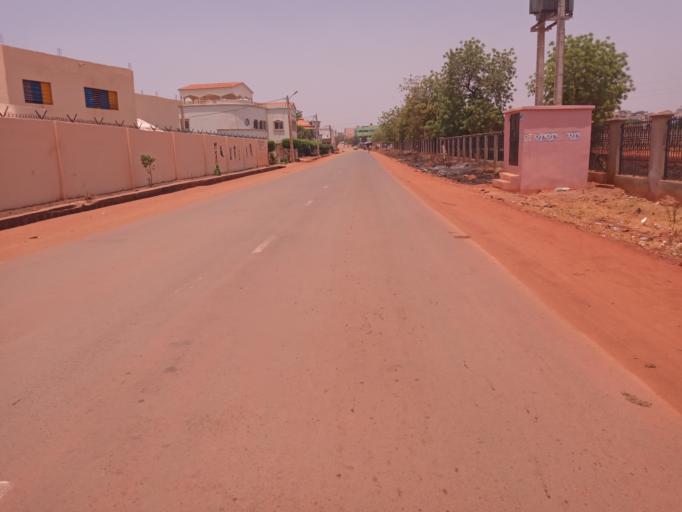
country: ML
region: Bamako
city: Bamako
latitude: 12.5885
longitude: -7.9334
